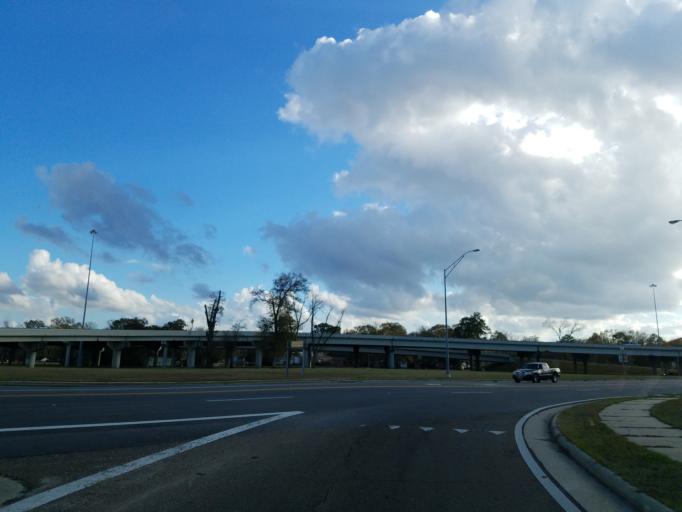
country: US
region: Mississippi
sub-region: Jones County
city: Laurel
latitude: 31.6861
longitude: -89.1376
